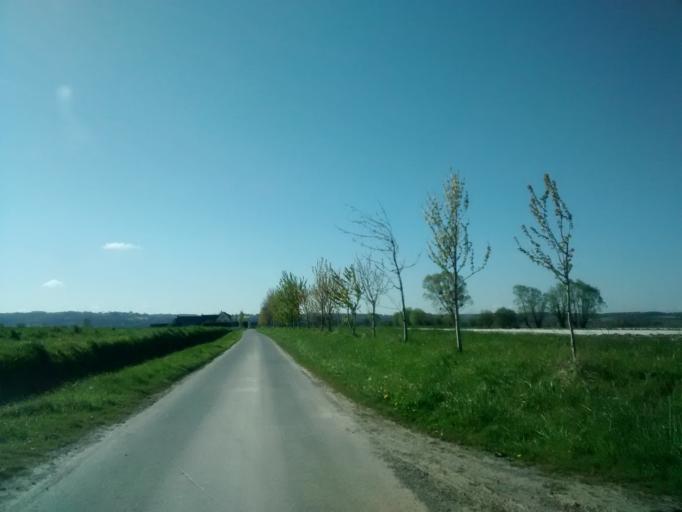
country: FR
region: Brittany
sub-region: Departement d'Ille-et-Vilaine
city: Saint-Broladre
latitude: 48.6067
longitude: -1.6759
